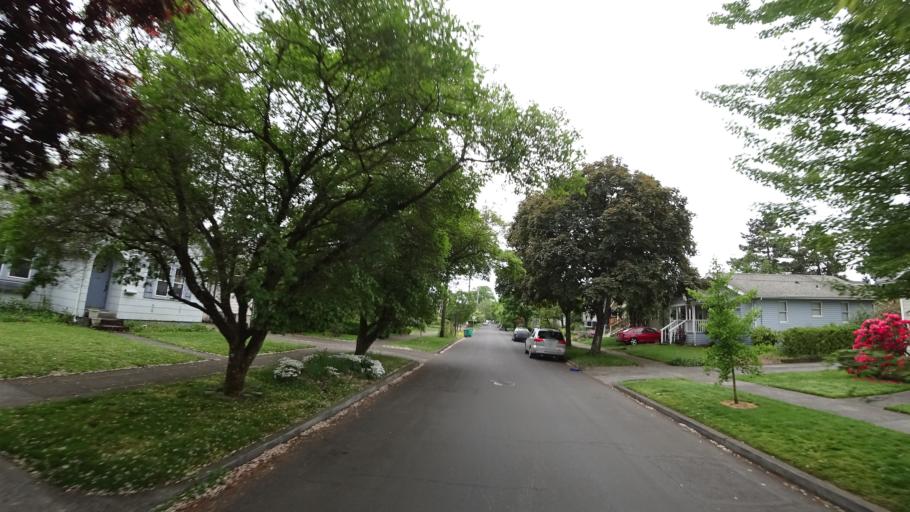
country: US
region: Oregon
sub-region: Multnomah County
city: Portland
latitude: 45.5477
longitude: -122.6117
